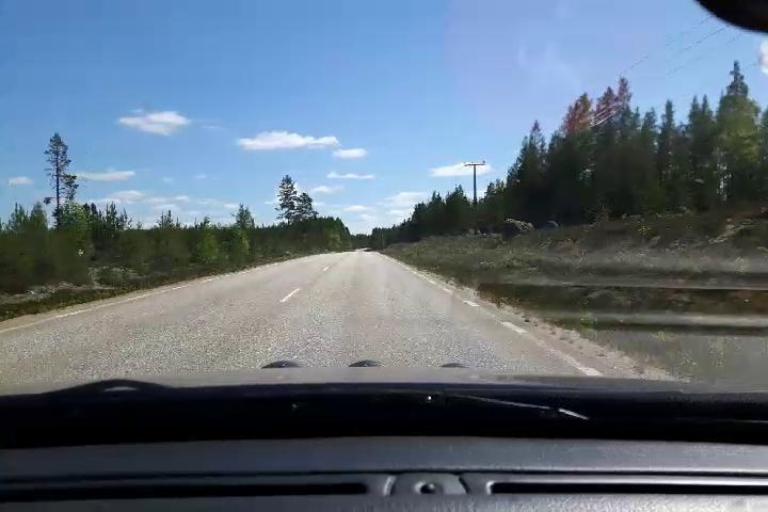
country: SE
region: Vaesternorrland
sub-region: Ange Kommun
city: Ange
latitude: 62.0949
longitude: 15.0837
